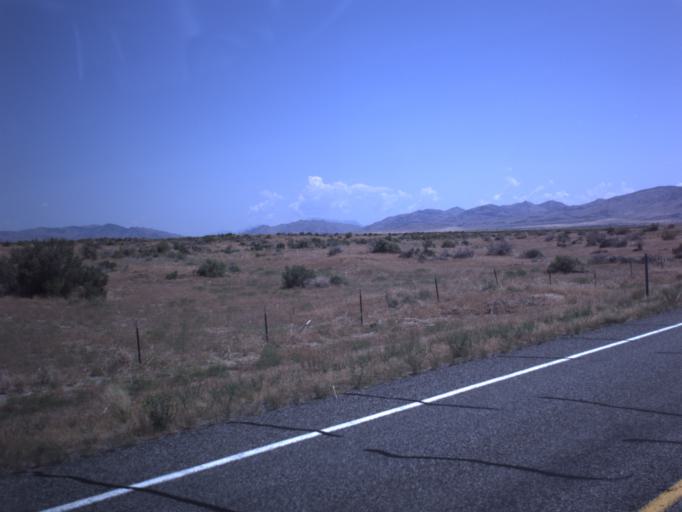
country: US
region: Utah
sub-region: Millard County
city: Delta
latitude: 39.3534
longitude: -112.4673
